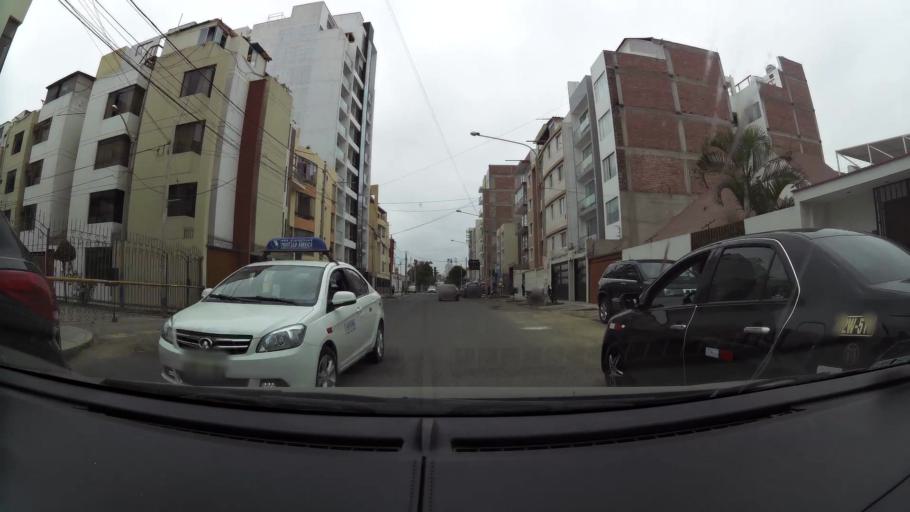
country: PE
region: La Libertad
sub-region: Provincia de Trujillo
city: Buenos Aires
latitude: -8.1362
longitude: -79.0390
